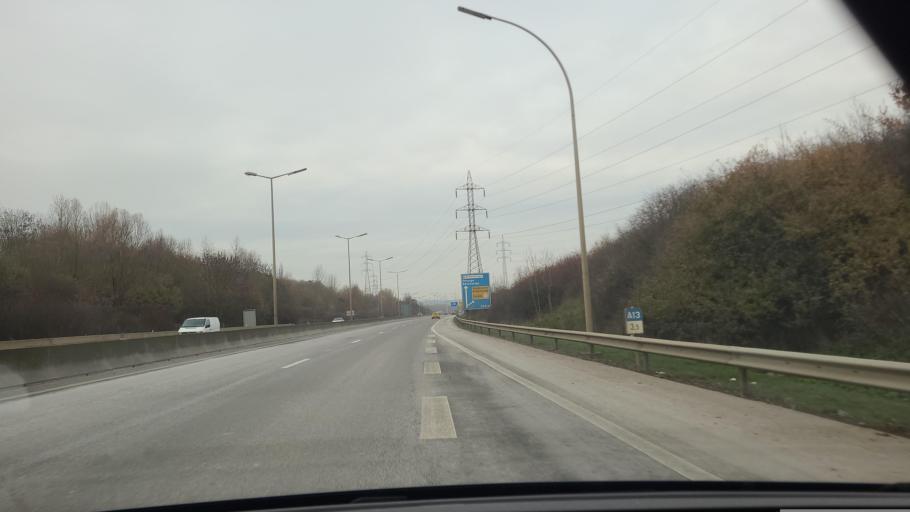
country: LU
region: Luxembourg
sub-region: Canton d'Esch-sur-Alzette
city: Sanem
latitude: 49.5366
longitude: 5.9249
